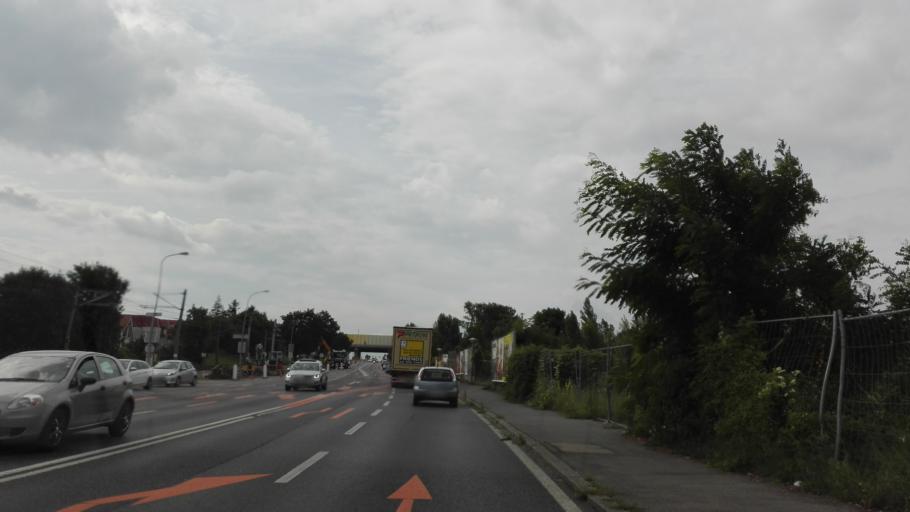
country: AT
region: Lower Austria
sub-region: Politischer Bezirk Modling
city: Vosendorf
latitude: 48.1250
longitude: 16.3186
